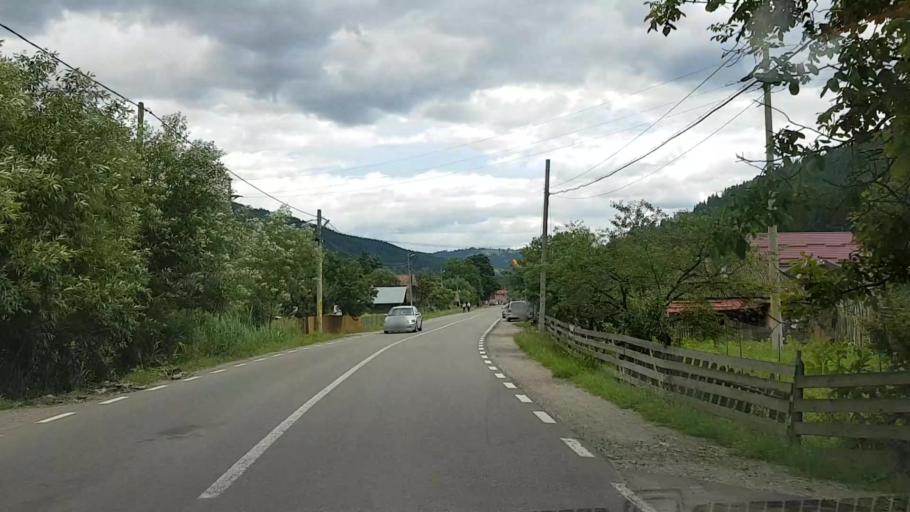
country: RO
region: Neamt
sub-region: Comuna Poiana Teiului
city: Poiana Teiului
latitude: 47.1169
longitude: 25.9199
